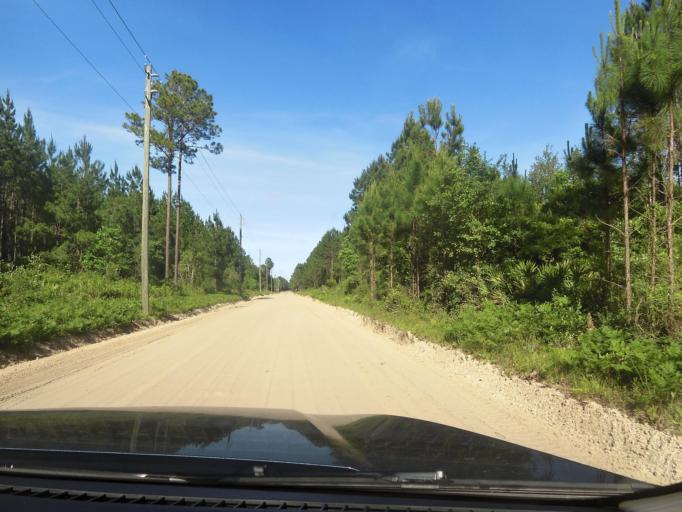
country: US
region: Florida
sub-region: Nassau County
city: Callahan
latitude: 30.5680
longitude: -81.7791
